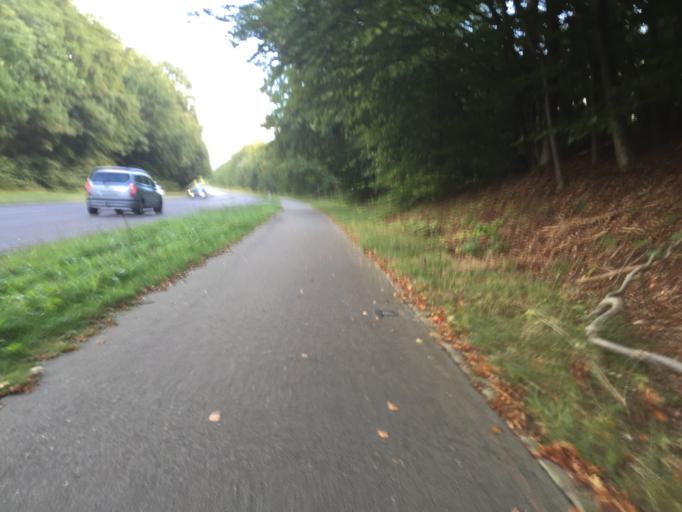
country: DK
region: Capital Region
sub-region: Fureso Kommune
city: Stavnsholt
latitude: 55.7755
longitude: 12.4106
